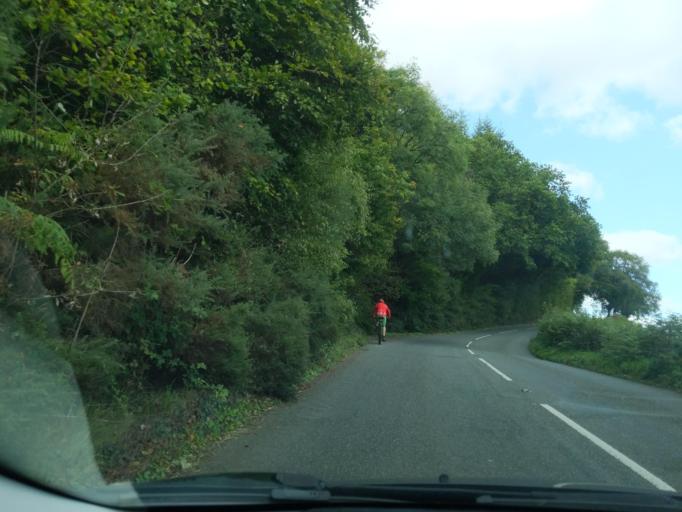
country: GB
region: England
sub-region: Devon
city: Chudleigh
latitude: 50.6040
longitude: -3.6203
